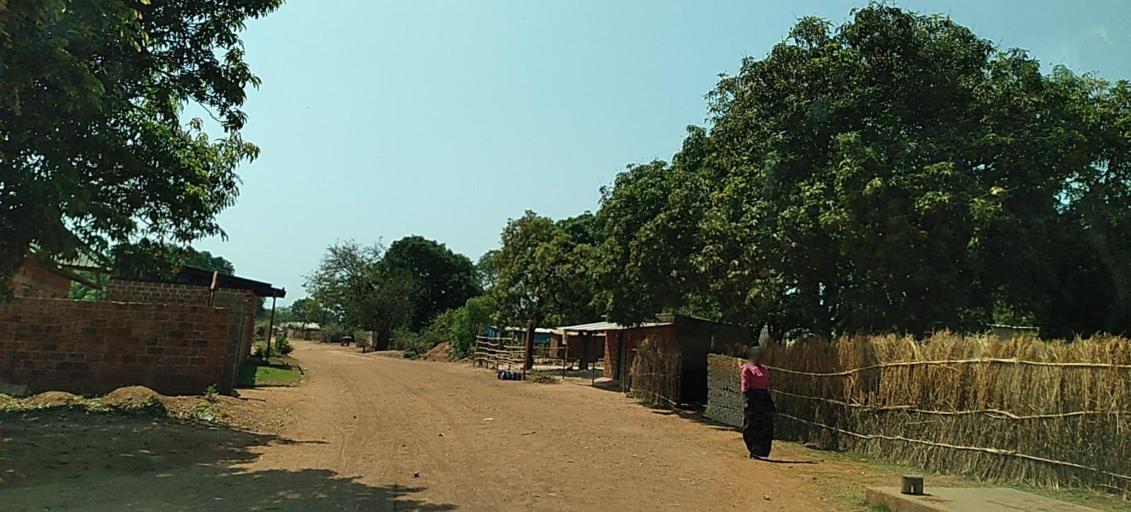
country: ZM
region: Copperbelt
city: Luanshya
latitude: -13.3539
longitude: 28.4131
